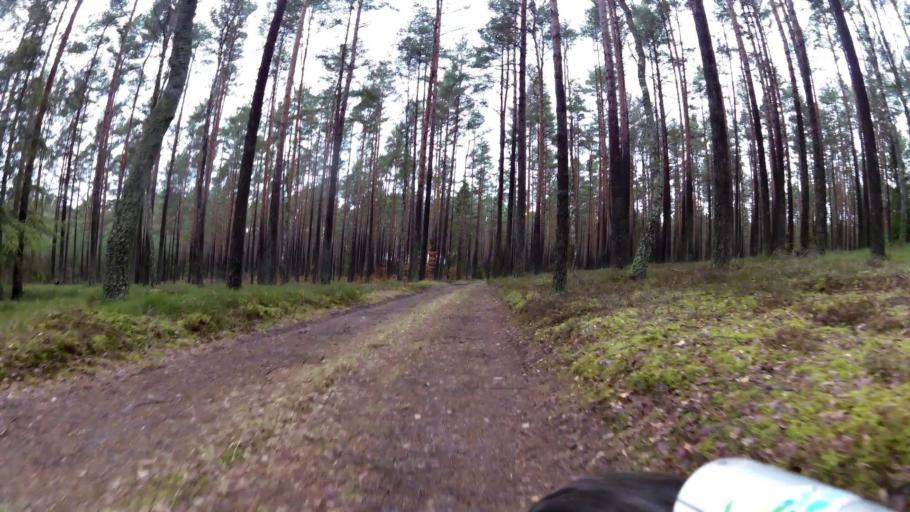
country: PL
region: Pomeranian Voivodeship
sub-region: Powiat bytowski
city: Borzytuchom
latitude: 54.2639
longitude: 17.3564
